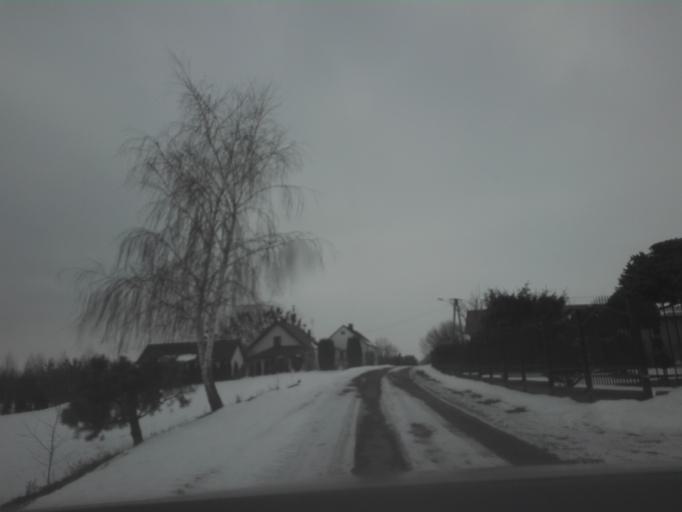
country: PL
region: Lublin Voivodeship
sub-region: Powiat hrubieszowski
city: Horodlo
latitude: 50.8409
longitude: 24.0166
